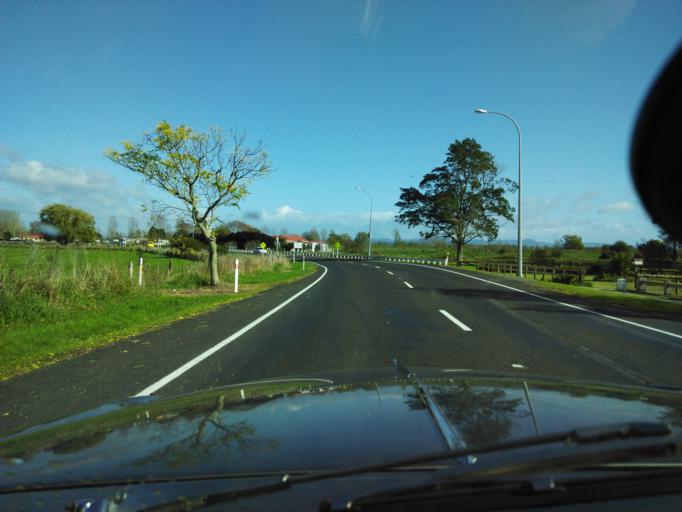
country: NZ
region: Waikato
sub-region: Hauraki District
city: Paeroa
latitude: -37.3860
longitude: 175.6684
